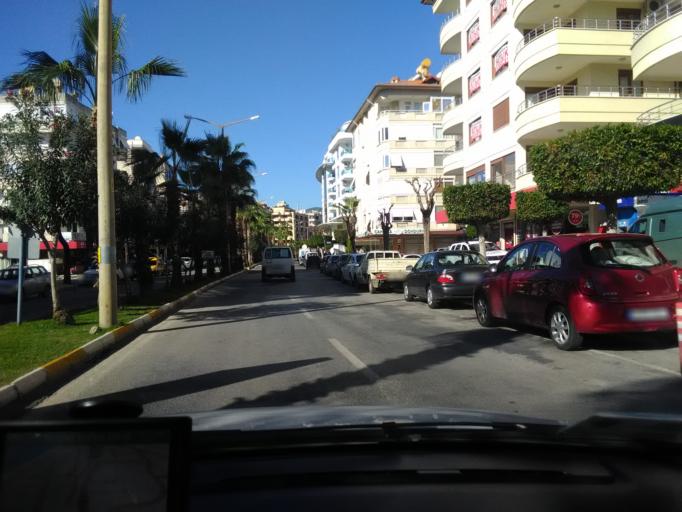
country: TR
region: Antalya
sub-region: Alanya
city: Alanya
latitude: 36.5476
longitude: 31.9927
